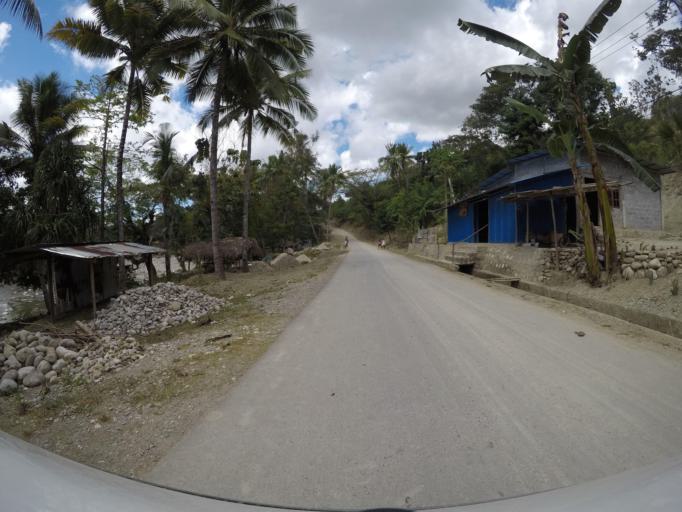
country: TL
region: Viqueque
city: Viqueque
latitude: -8.8741
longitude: 126.3642
